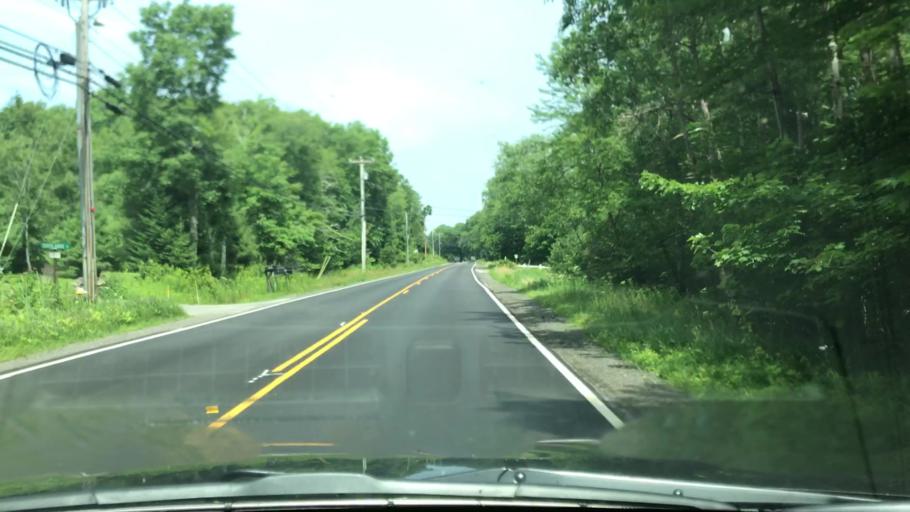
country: US
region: Maine
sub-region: Waldo County
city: Lincolnville
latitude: 44.2565
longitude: -69.0266
